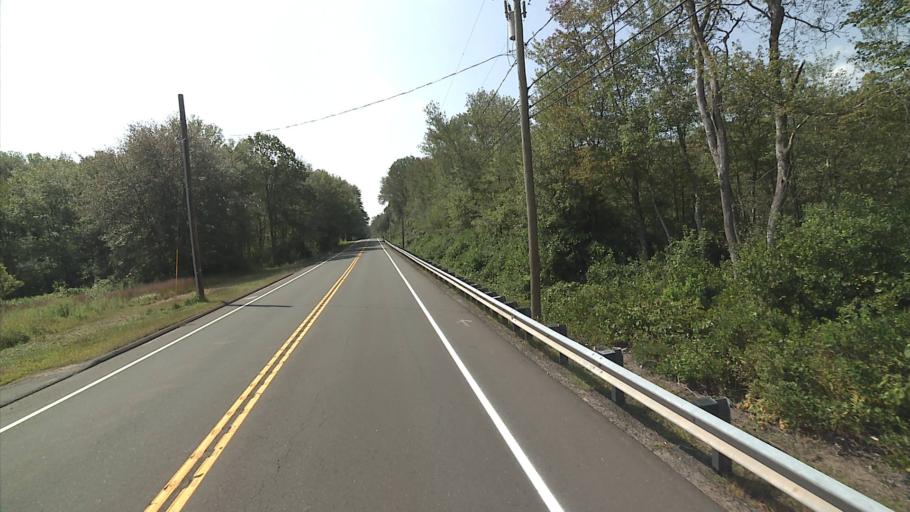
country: US
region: Connecticut
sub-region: Middlesex County
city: Durham
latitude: 41.4268
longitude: -72.6501
